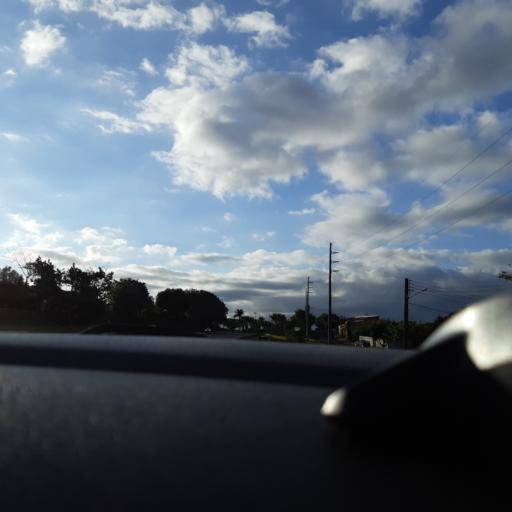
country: BR
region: Sao Paulo
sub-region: Ourinhos
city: Ourinhos
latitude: -22.9881
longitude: -49.8546
